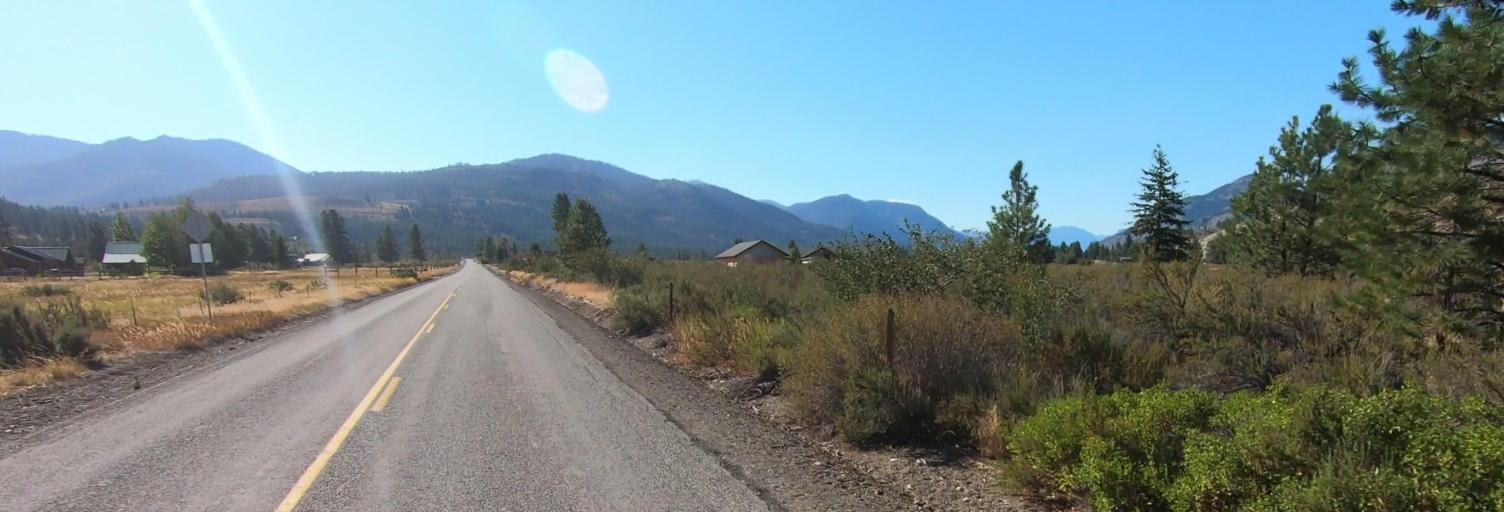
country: US
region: Washington
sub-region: Chelan County
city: Granite Falls
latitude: 48.4906
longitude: -120.2343
